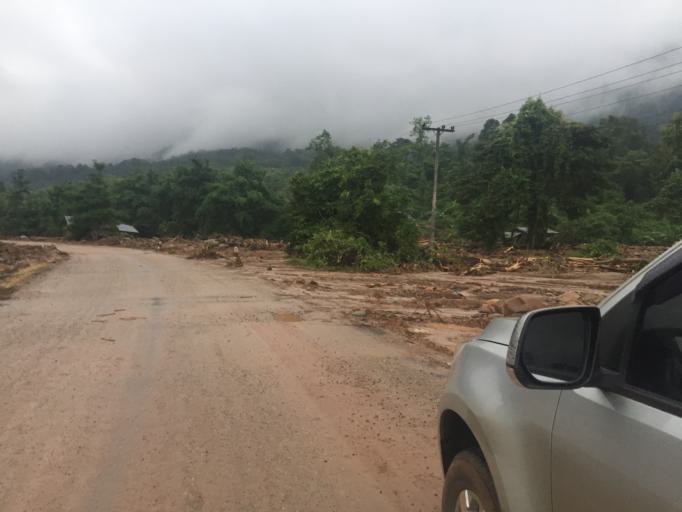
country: LA
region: Attapu
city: Attapu
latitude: 15.0912
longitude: 106.8262
